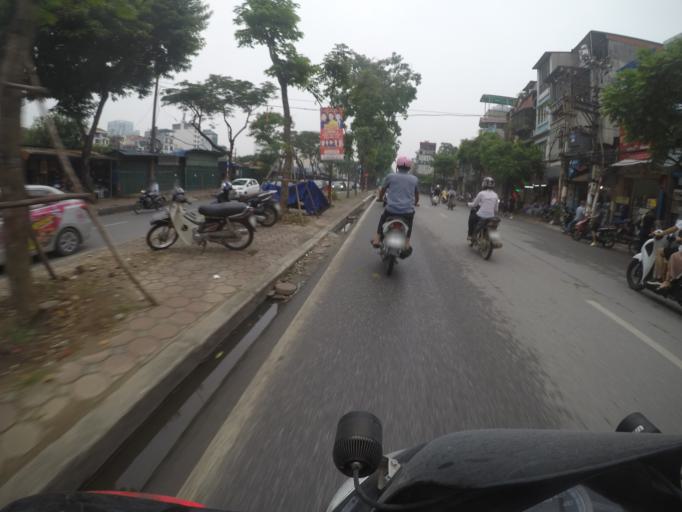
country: VN
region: Ha Noi
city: Thanh Xuan
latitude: 21.0094
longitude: 105.8135
